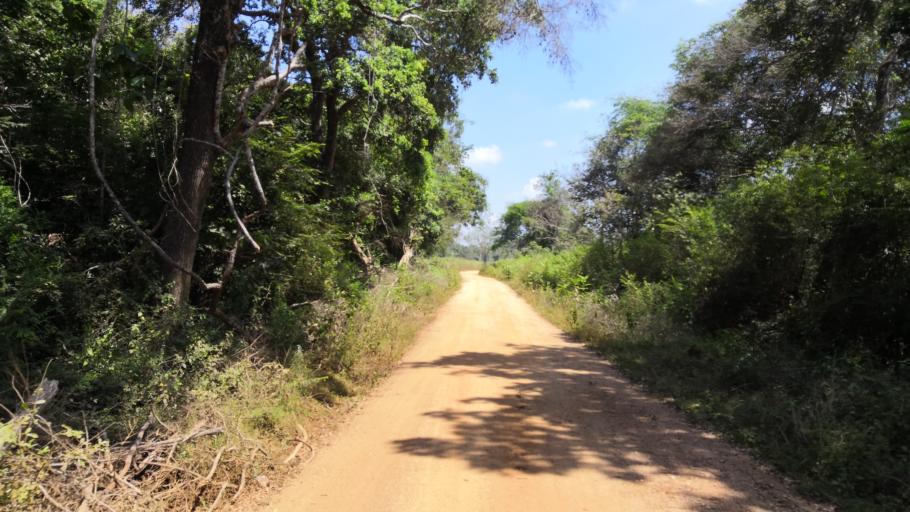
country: LK
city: Padaviya Divisional Secretariat
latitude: 8.9691
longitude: 80.6876
